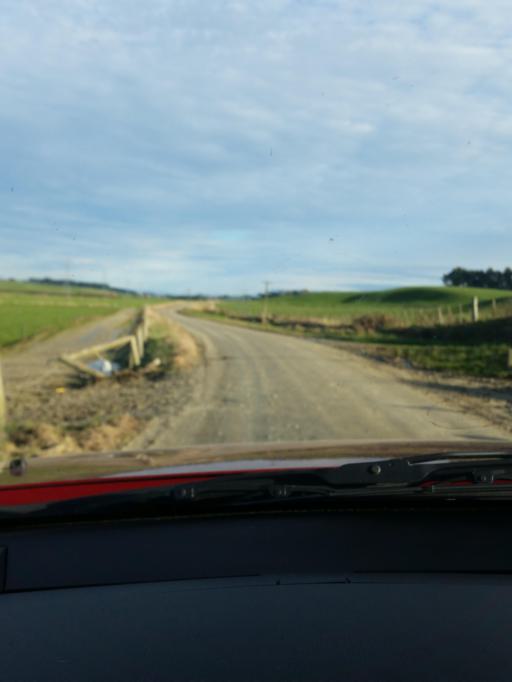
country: NZ
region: Southland
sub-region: Gore District
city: Gore
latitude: -46.2099
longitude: 168.7603
